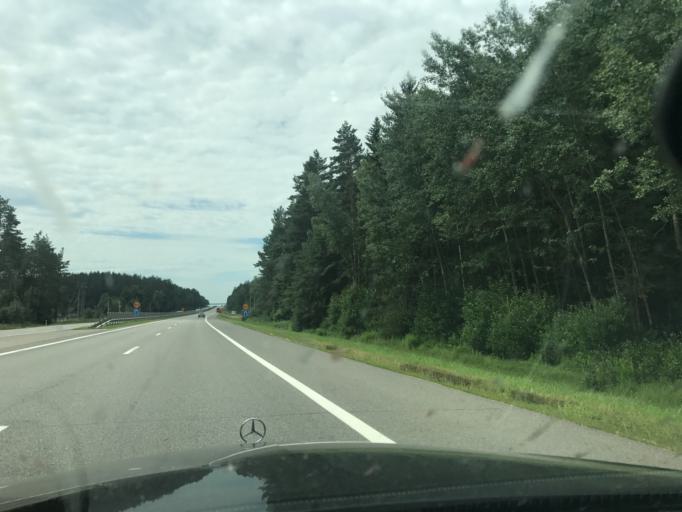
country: BY
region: Minsk
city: Zamostochcha
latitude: 53.8703
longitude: 27.9213
